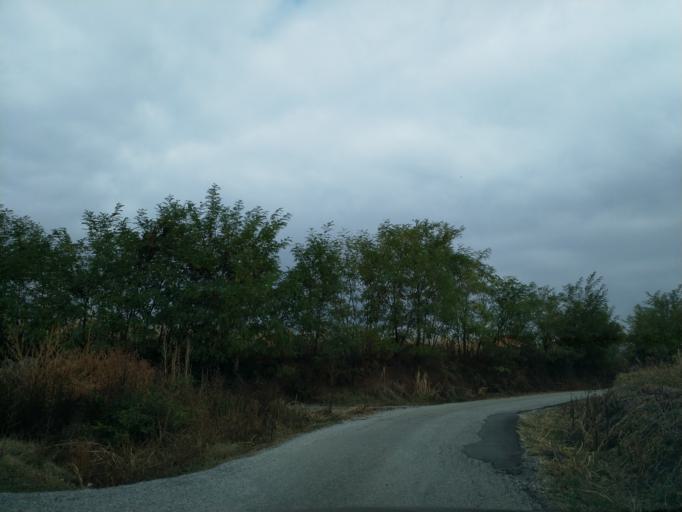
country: RS
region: Central Serbia
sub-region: Sumadijski Okrug
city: Arangelovac
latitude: 44.3080
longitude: 20.5897
